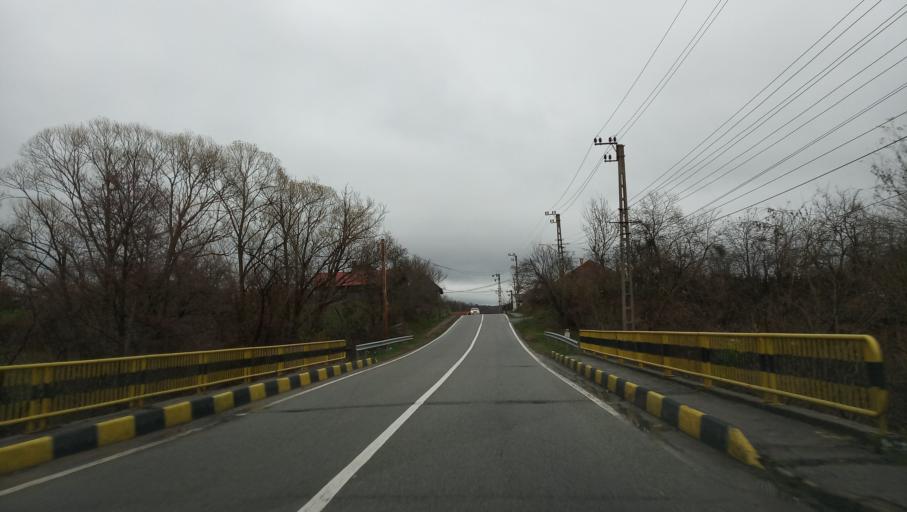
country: RO
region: Gorj
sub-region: Novaci
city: Pociovalistea
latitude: 45.1538
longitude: 23.6350
